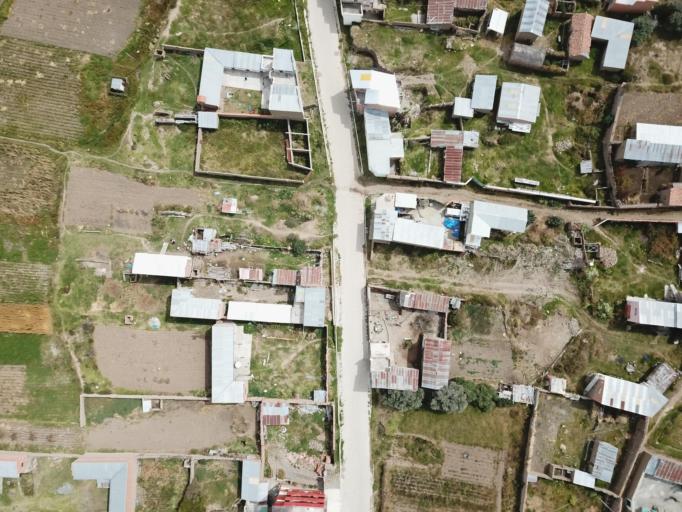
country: BO
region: La Paz
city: Achacachi
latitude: -16.0532
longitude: -68.8139
